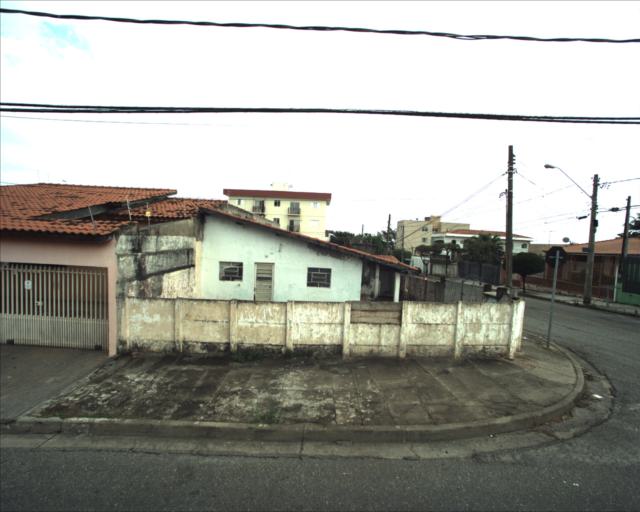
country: BR
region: Sao Paulo
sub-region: Sorocaba
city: Sorocaba
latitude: -23.5068
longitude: -47.4942
